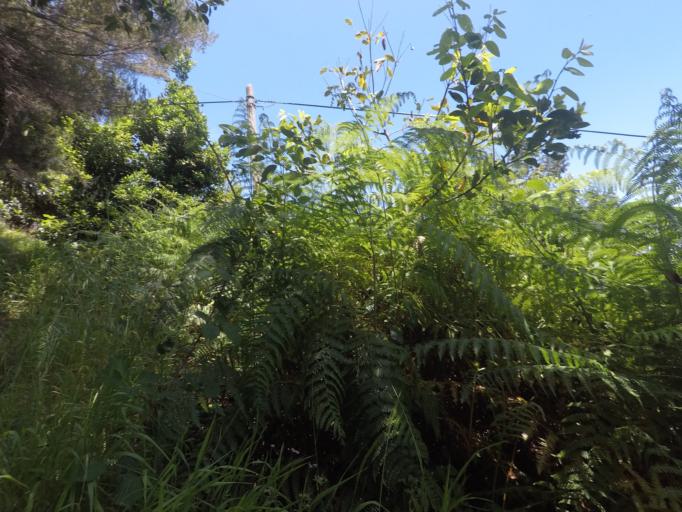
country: PT
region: Madeira
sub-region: Porto Moniz
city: Porto Moniz
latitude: 32.8313
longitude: -17.1345
